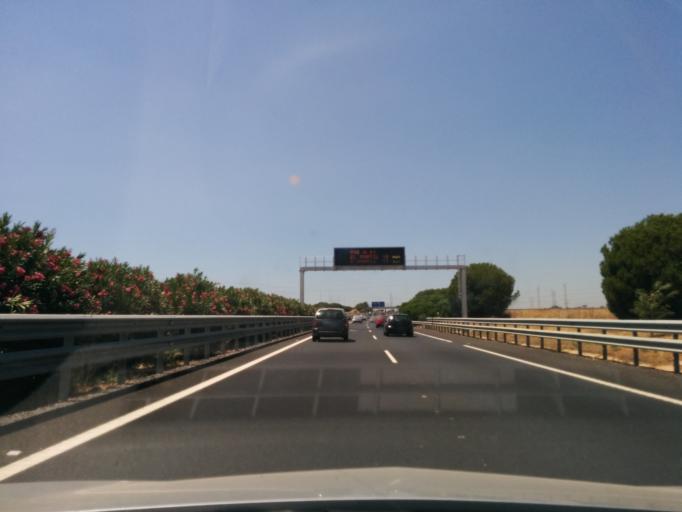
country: ES
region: Andalusia
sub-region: Provincia de Huelva
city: San Juan del Puerto
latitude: 37.3176
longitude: -6.8589
